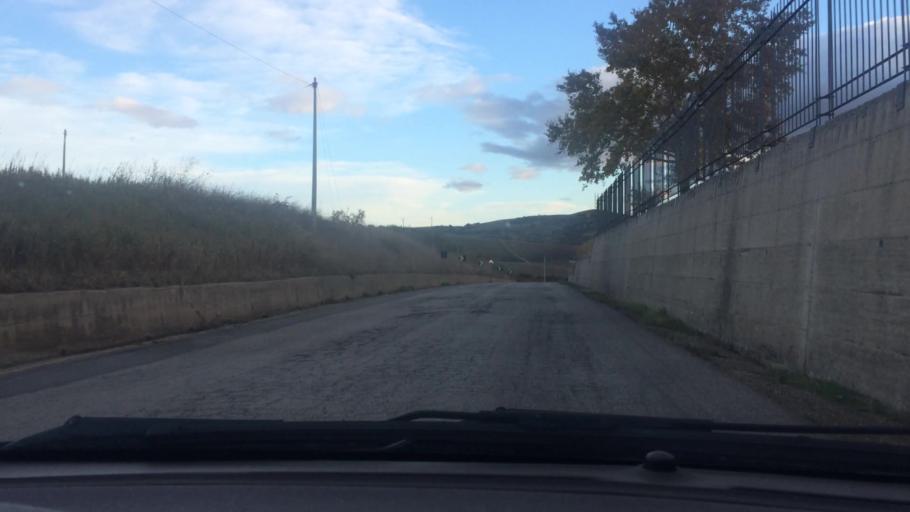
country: IT
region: Basilicate
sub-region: Provincia di Potenza
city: Tolve
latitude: 40.7109
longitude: 16.0195
